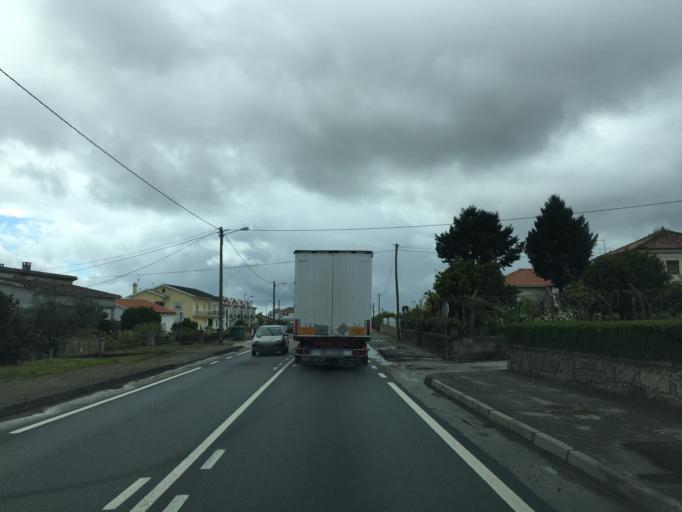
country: PT
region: Coimbra
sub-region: Oliveira do Hospital
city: Oliveira do Hospital
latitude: 40.3153
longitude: -7.9024
